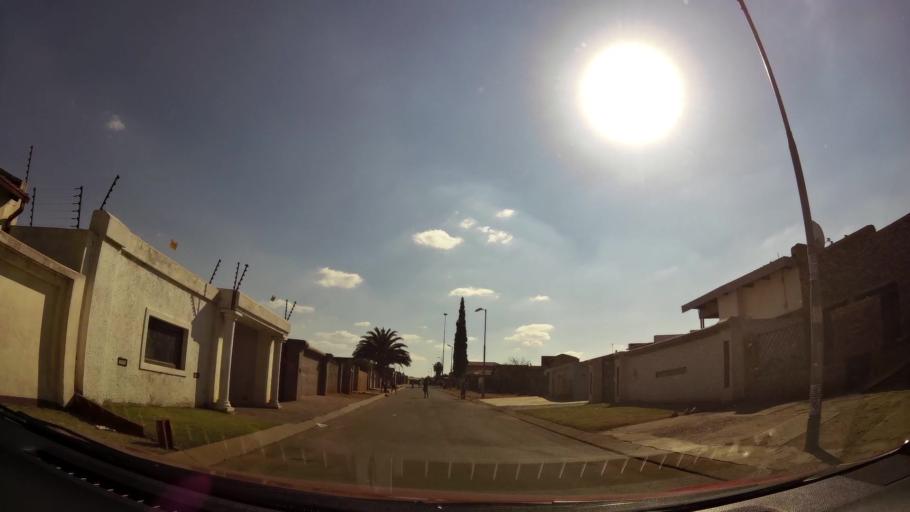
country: ZA
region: Gauteng
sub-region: City of Johannesburg Metropolitan Municipality
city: Soweto
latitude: -26.2352
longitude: 27.8816
